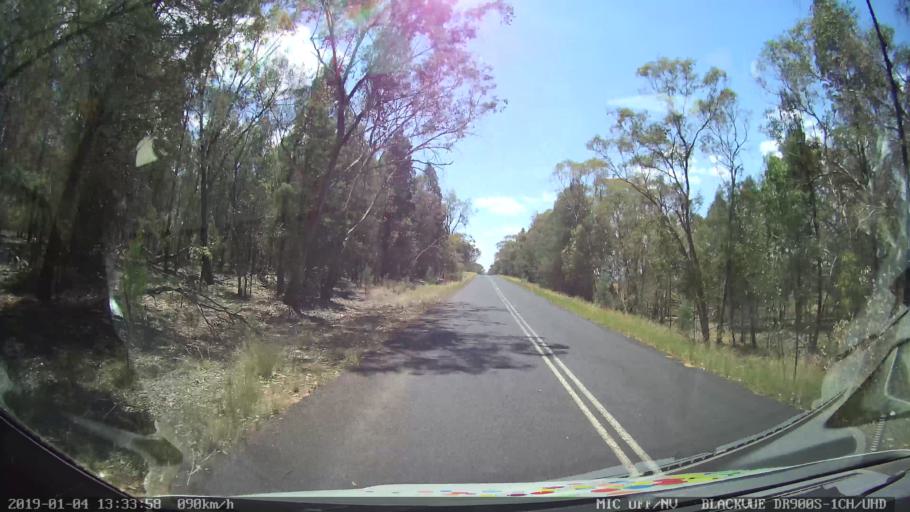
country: AU
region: New South Wales
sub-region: Dubbo Municipality
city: Dubbo
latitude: -32.5919
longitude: 148.5375
